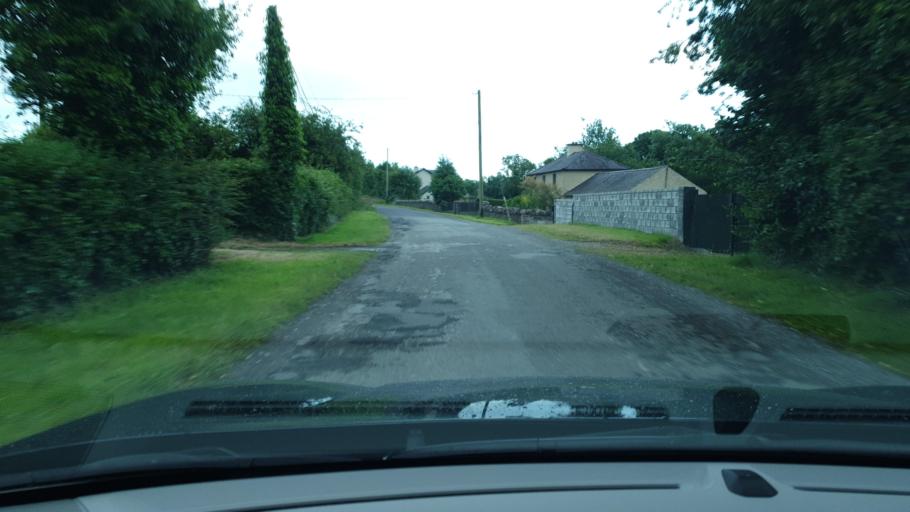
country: IE
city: Kentstown
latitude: 53.5937
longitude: -6.5778
